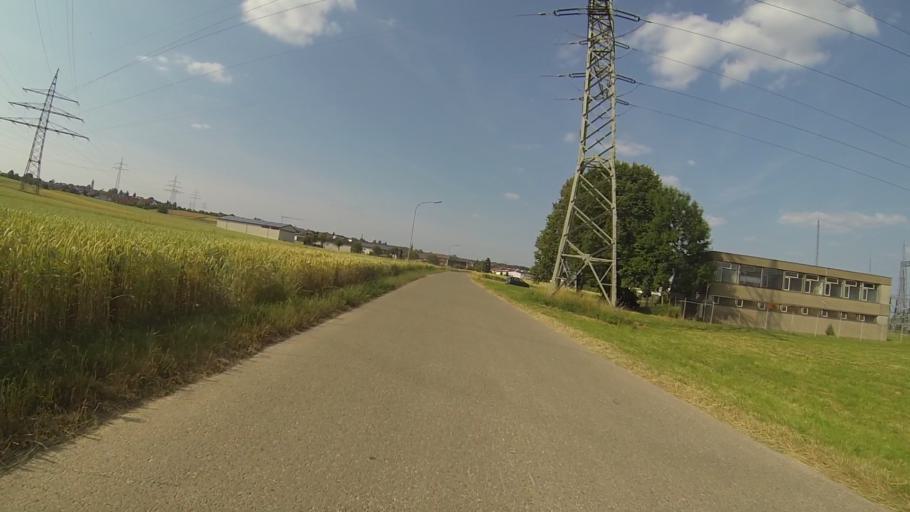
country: DE
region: Baden-Wuerttemberg
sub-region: Regierungsbezirk Stuttgart
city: Niederstotzingen
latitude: 48.5299
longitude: 10.2303
